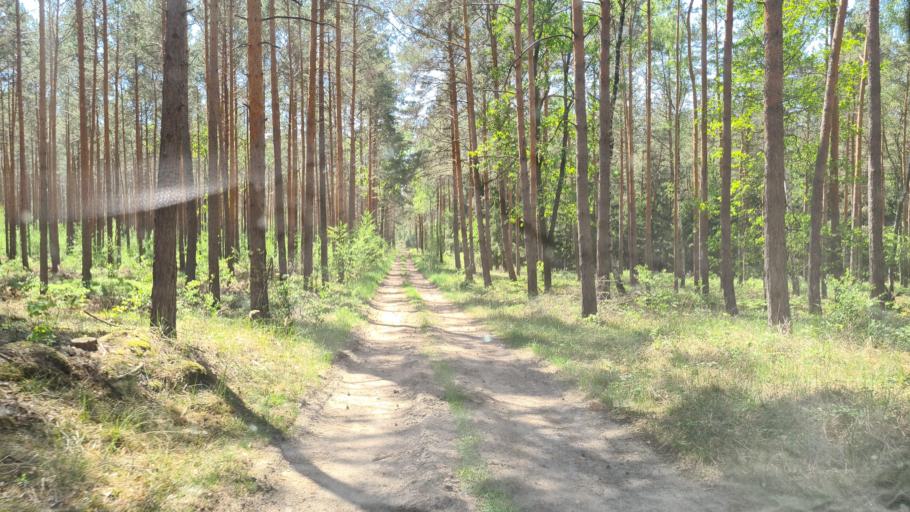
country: DE
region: Brandenburg
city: Sallgast
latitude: 51.5847
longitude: 13.8769
